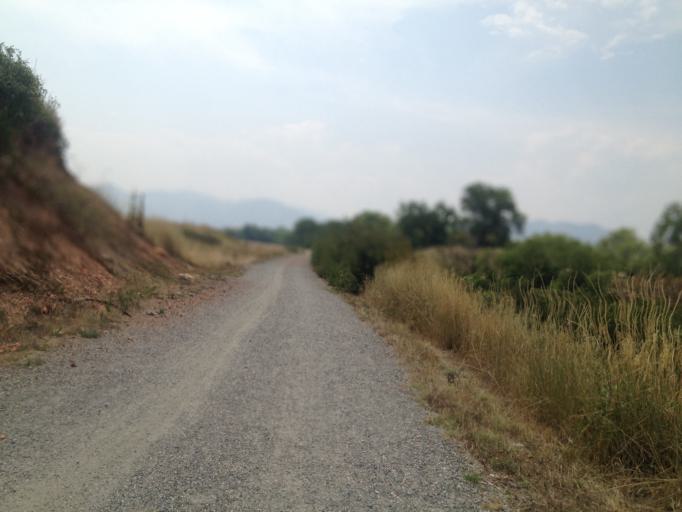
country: US
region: Colorado
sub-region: Boulder County
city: Superior
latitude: 39.9488
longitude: -105.1706
